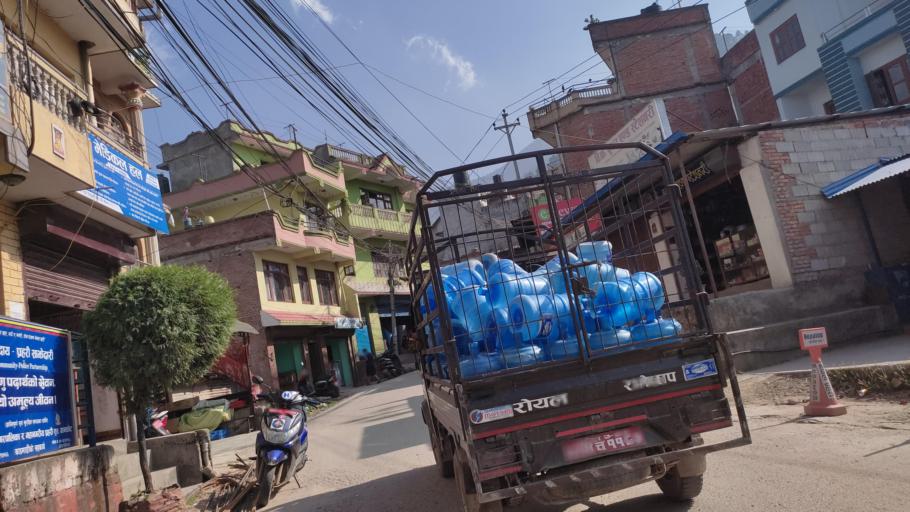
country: NP
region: Central Region
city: Kirtipur
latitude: 27.6707
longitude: 85.2502
